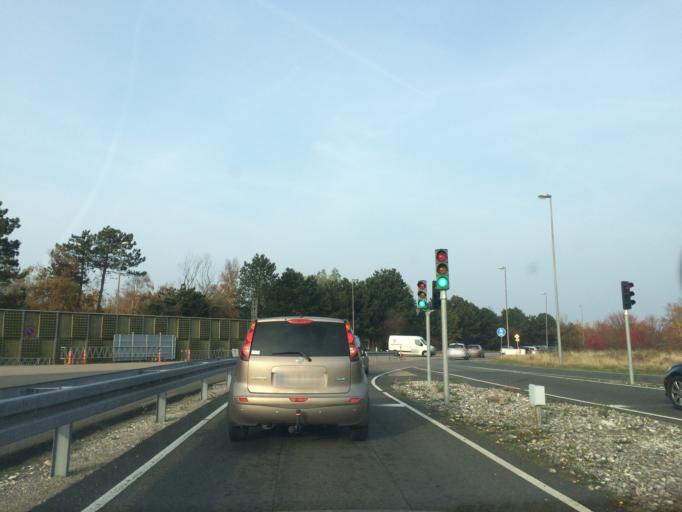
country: DK
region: Zealand
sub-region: Odsherred Kommune
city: Asnaes
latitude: 55.9773
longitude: 11.3015
